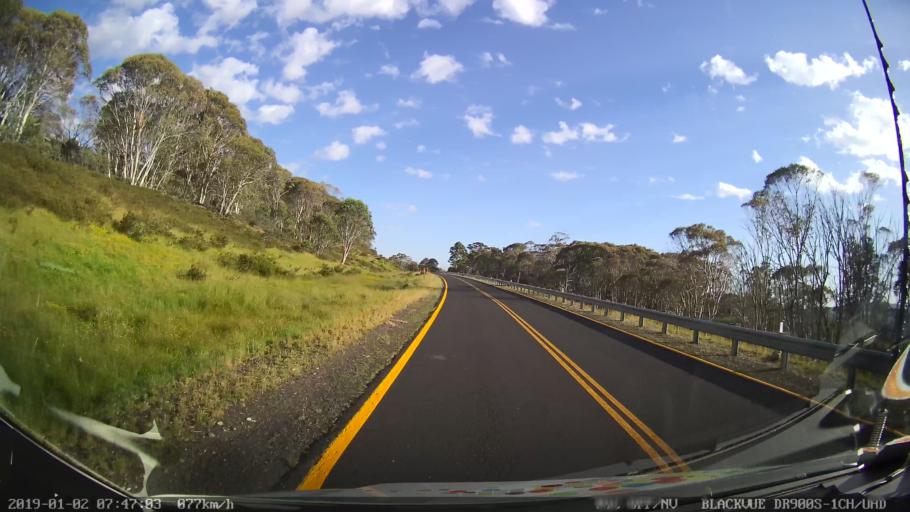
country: AU
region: New South Wales
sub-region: Tumut Shire
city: Tumut
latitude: -35.7690
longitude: 148.5215
